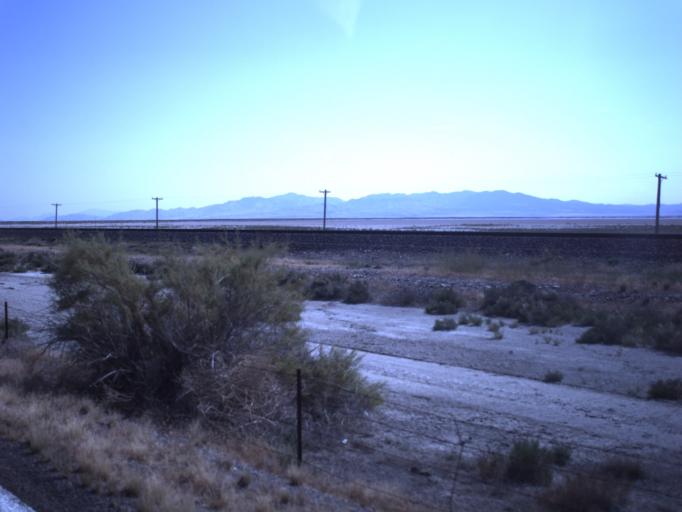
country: US
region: Utah
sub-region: Millard County
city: Delta
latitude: 39.1763
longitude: -112.7029
